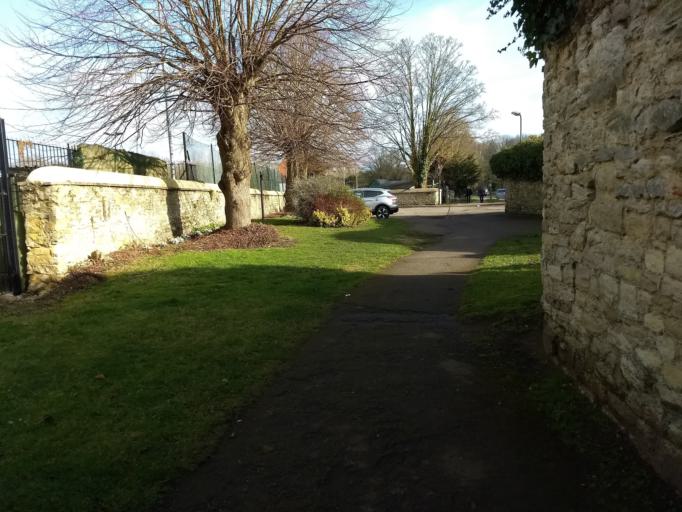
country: GB
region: England
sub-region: Milton Keynes
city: Stony Stratford
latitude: 52.0590
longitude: -0.8542
